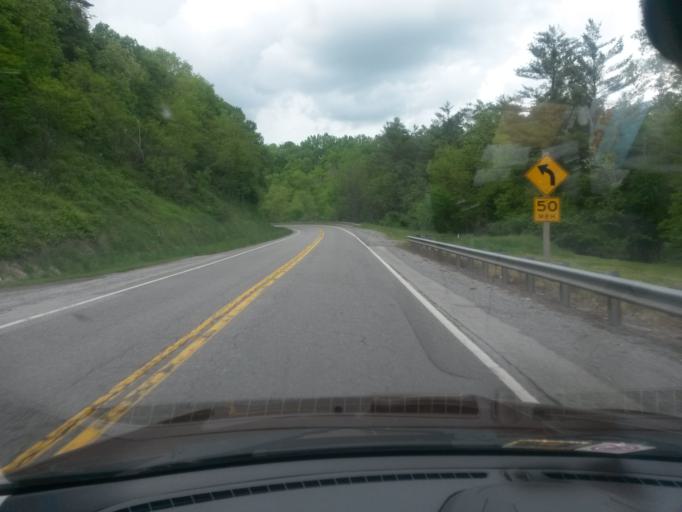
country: US
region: Virginia
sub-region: Floyd County
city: Floyd
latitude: 36.9289
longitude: -80.3314
